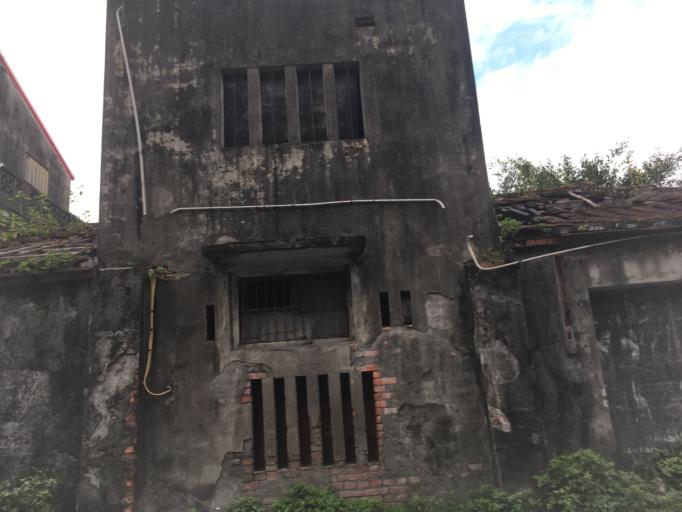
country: TW
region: Taiwan
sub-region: Yilan
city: Yilan
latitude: 24.6933
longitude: 121.7294
